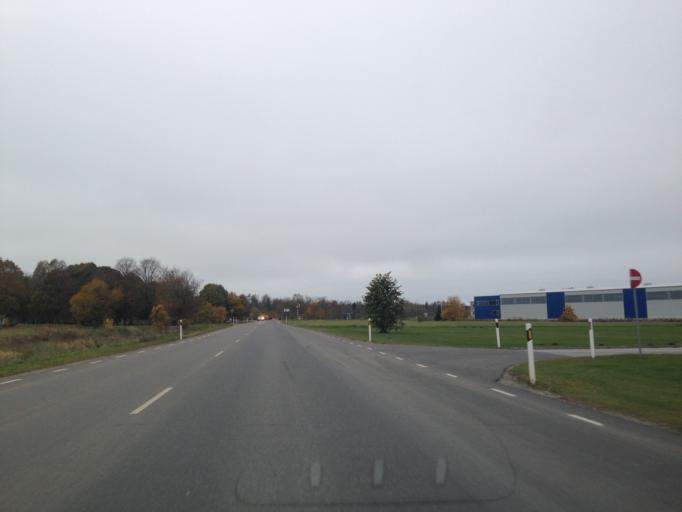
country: EE
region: Harju
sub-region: Harku vald
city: Tabasalu
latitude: 59.4195
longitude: 24.5409
